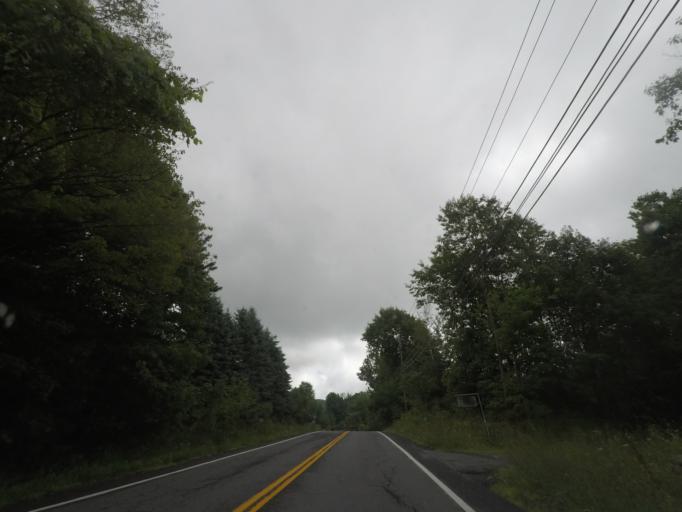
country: US
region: New York
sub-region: Rensselaer County
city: Averill Park
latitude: 42.5829
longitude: -73.4819
